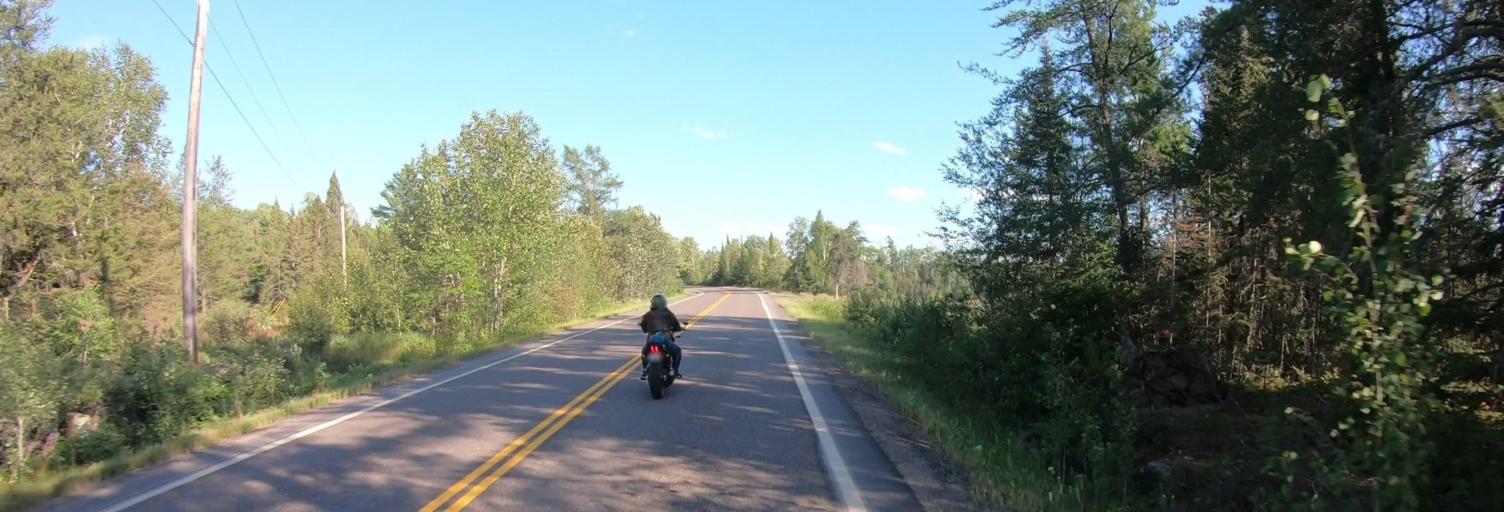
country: US
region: Minnesota
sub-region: Saint Louis County
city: Ely
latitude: 47.9601
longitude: -91.5566
